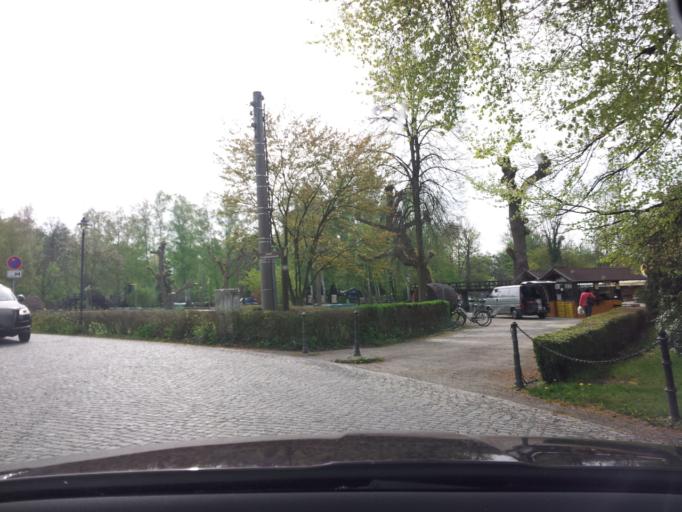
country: DE
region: Brandenburg
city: Lubbenau
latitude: 51.8680
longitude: 13.9735
